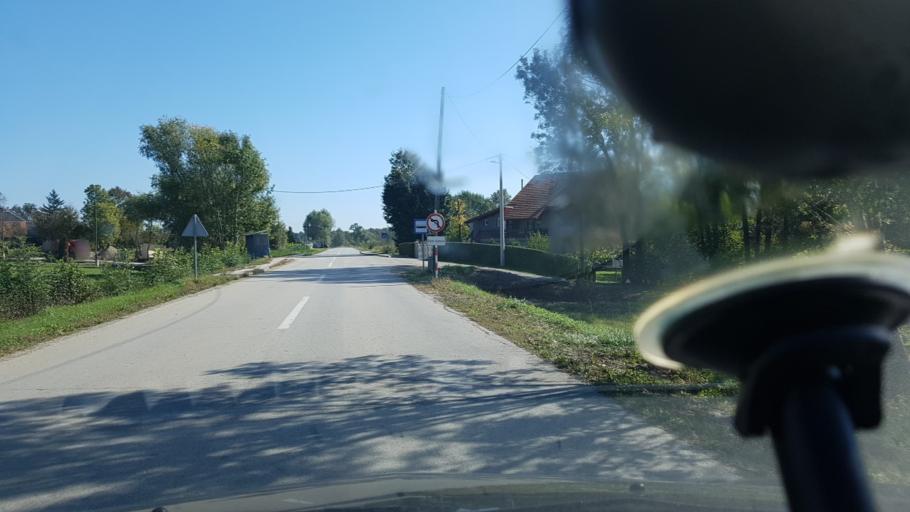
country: HR
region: Zagrebacka
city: Brckovljani
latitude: 45.7601
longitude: 16.2561
